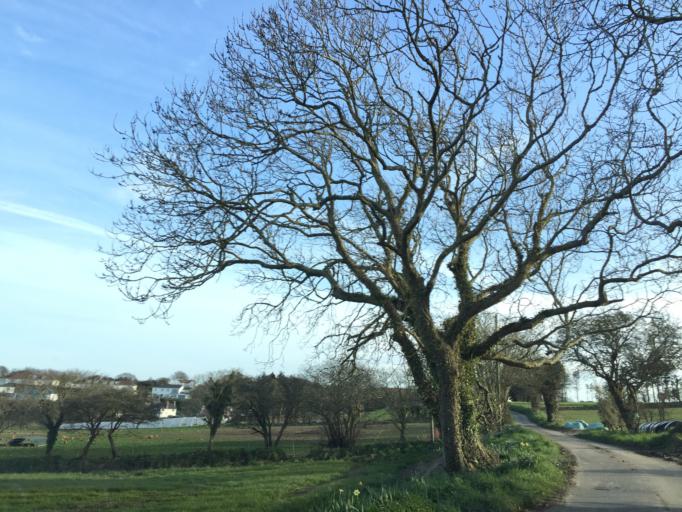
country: JE
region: St Helier
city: Saint Helier
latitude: 49.2477
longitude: -2.0981
